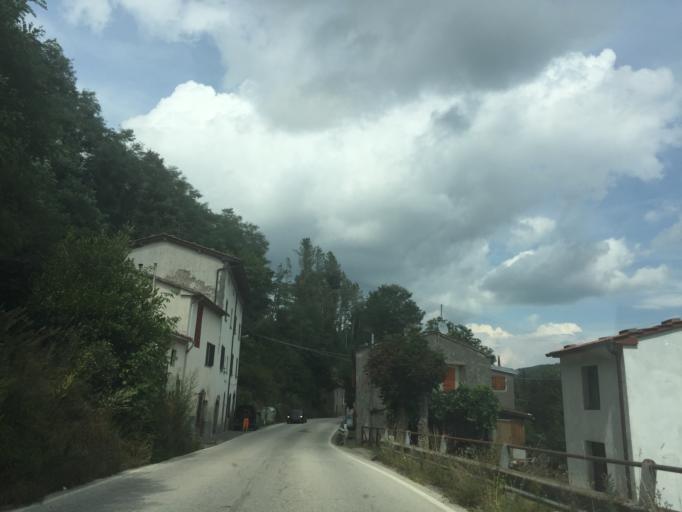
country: IT
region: Tuscany
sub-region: Provincia di Pistoia
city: Campo Tizzoro
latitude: 44.0124
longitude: 10.8570
